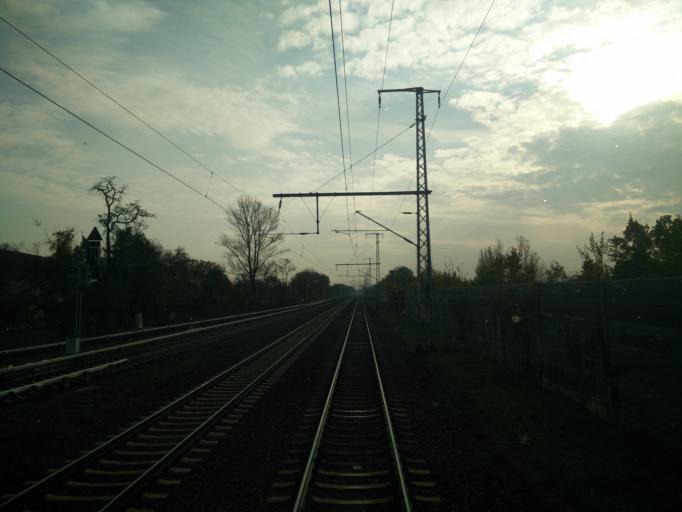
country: DE
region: Berlin
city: Karlshorst
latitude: 52.4780
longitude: 13.5324
